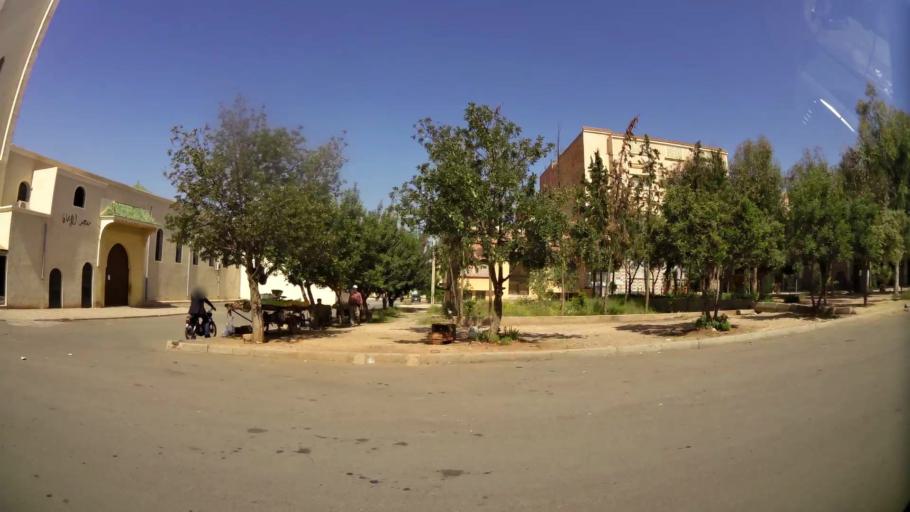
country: MA
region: Oriental
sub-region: Oujda-Angad
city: Oujda
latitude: 34.6914
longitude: -1.8741
